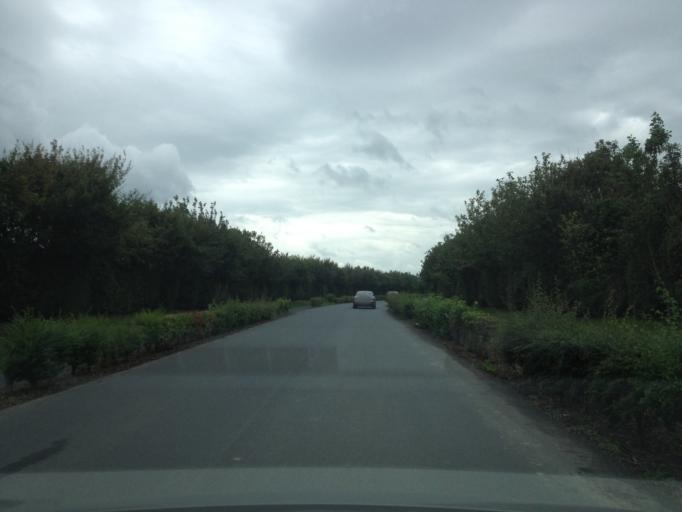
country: FR
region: Lower Normandy
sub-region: Departement du Calvados
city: Grandcamp-Maisy
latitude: 49.3920
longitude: -0.9903
